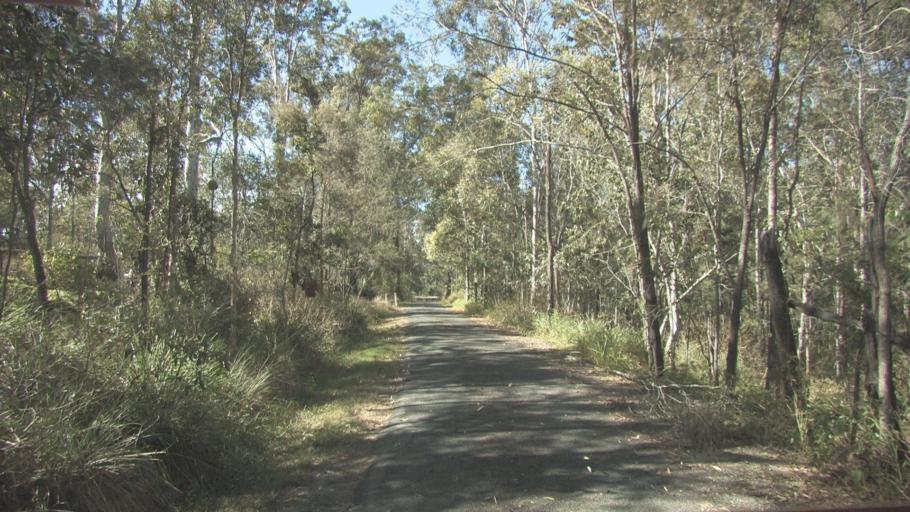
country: AU
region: Queensland
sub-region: Ipswich
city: Springfield Lakes
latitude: -27.7092
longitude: 152.9451
